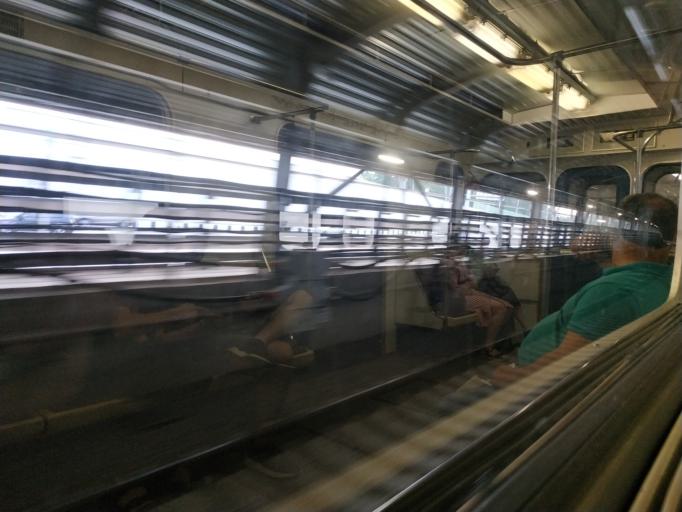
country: RU
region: Moskovskaya
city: Kommunarka
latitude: 55.5667
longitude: 37.4611
